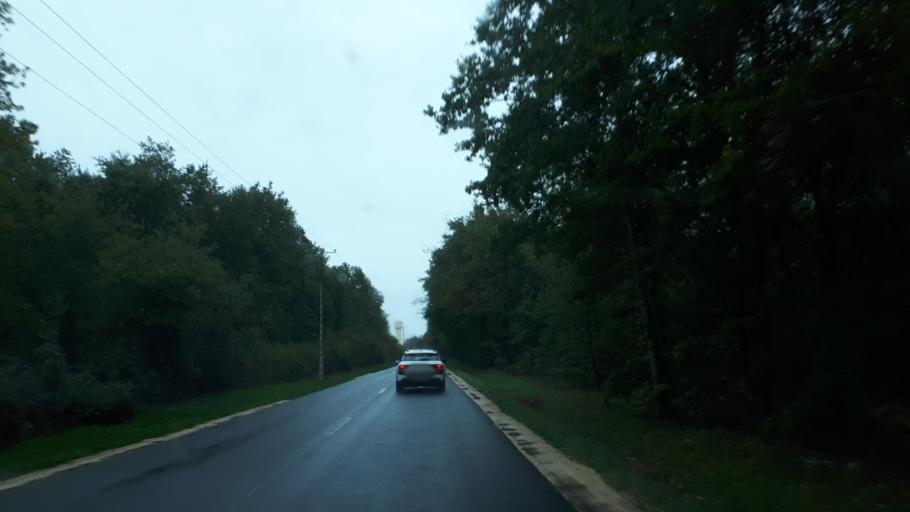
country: FR
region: Centre
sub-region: Departement du Loir-et-Cher
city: Gievres
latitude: 47.2935
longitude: 1.6713
